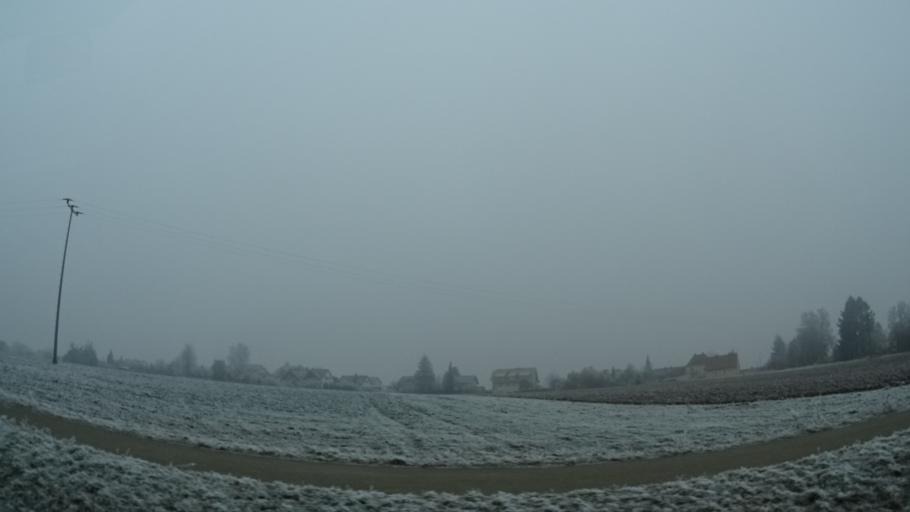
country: DE
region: Bavaria
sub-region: Regierungsbezirk Unterfranken
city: Hassfurt
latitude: 50.0468
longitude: 10.5232
